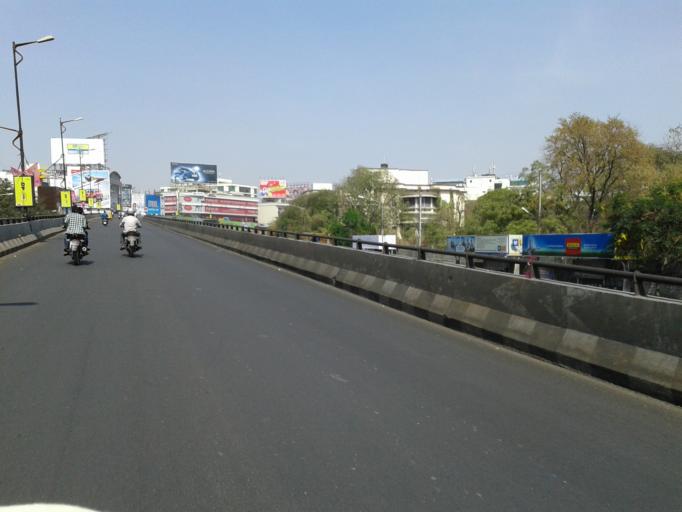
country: IN
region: Telangana
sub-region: Hyderabad
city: Hyderabad
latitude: 17.4331
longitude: 78.4558
